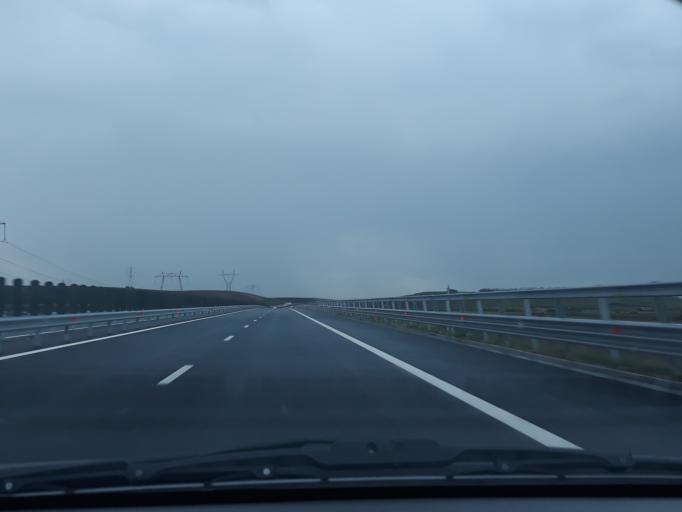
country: RO
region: Mures
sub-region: Comuna Sanpaul
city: Sanpaul
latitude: 46.4418
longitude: 24.3470
